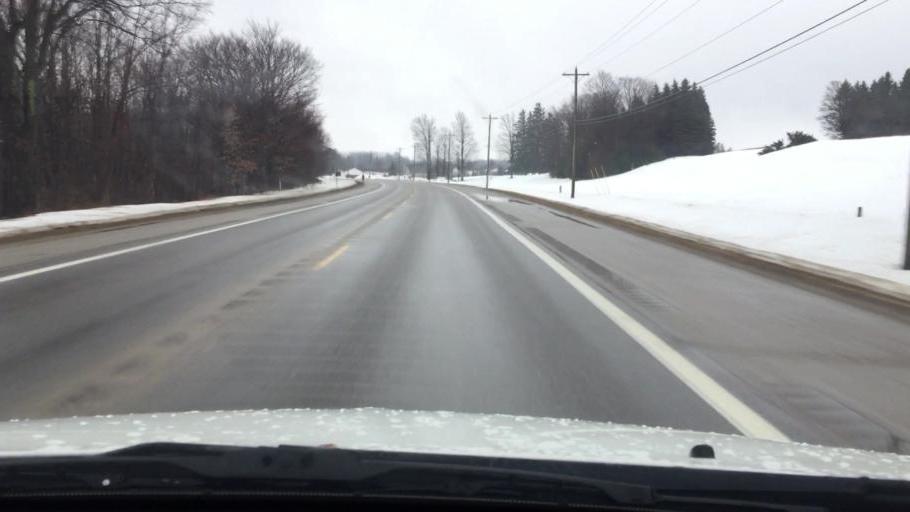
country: US
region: Michigan
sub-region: Charlevoix County
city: Charlevoix
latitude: 45.2844
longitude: -85.2416
